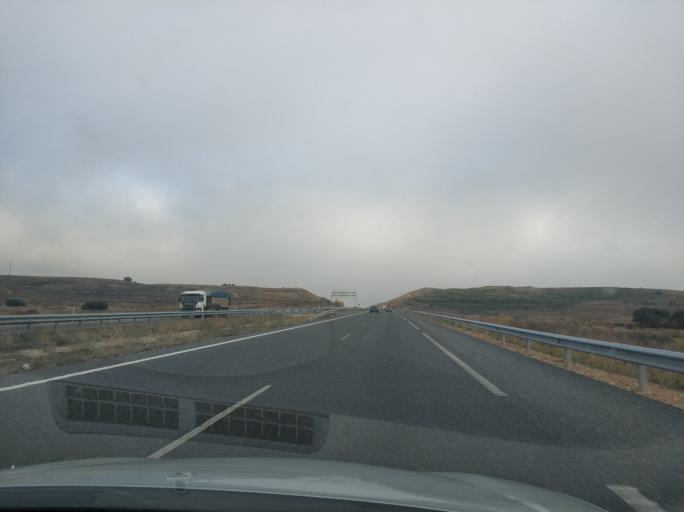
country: ES
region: Castille and Leon
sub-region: Provincia de Leon
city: Leon
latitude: 42.5642
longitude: -5.5383
